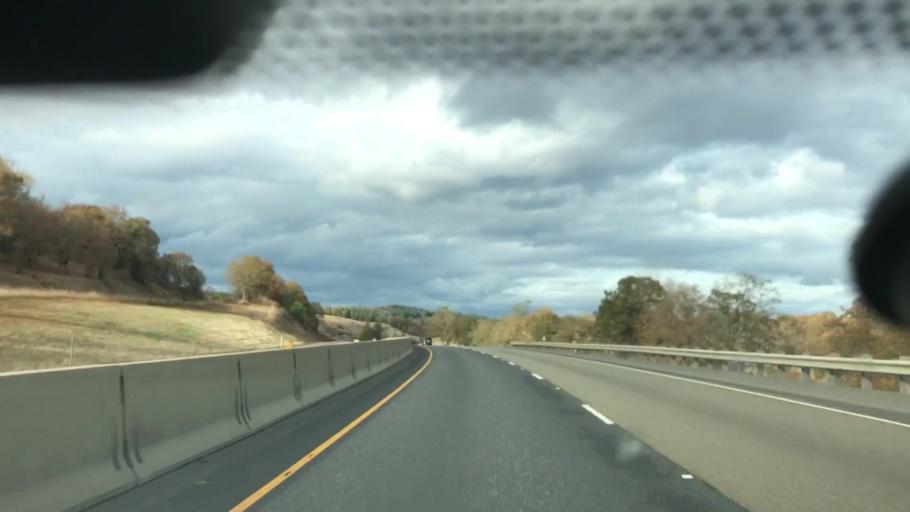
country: US
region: Oregon
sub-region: Douglas County
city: Sutherlin
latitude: 43.4249
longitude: -123.3191
